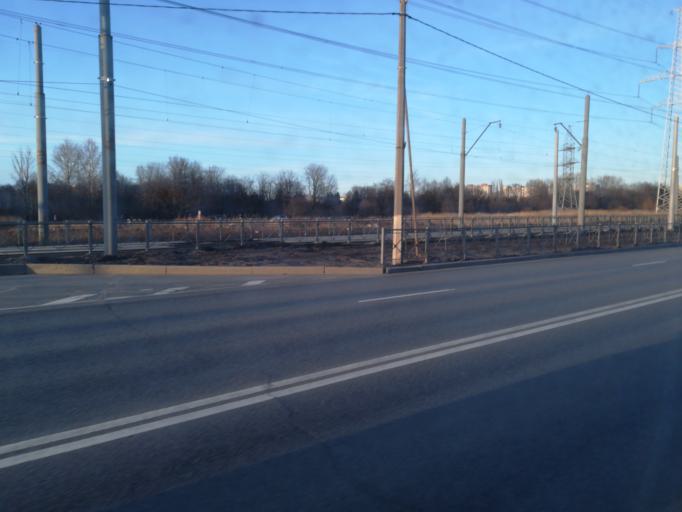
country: RU
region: St.-Petersburg
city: Sosnovaya Polyana
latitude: 59.8466
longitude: 30.1592
